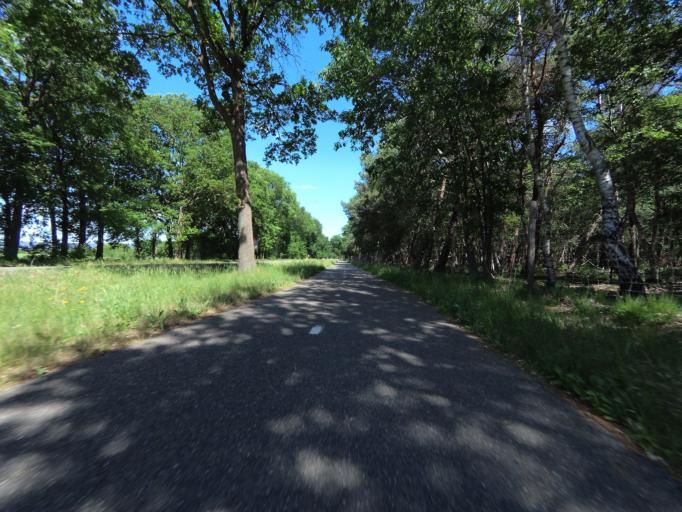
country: NL
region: Gelderland
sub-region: Gemeente Ede
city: Otterlo
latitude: 52.1148
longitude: 5.7664
